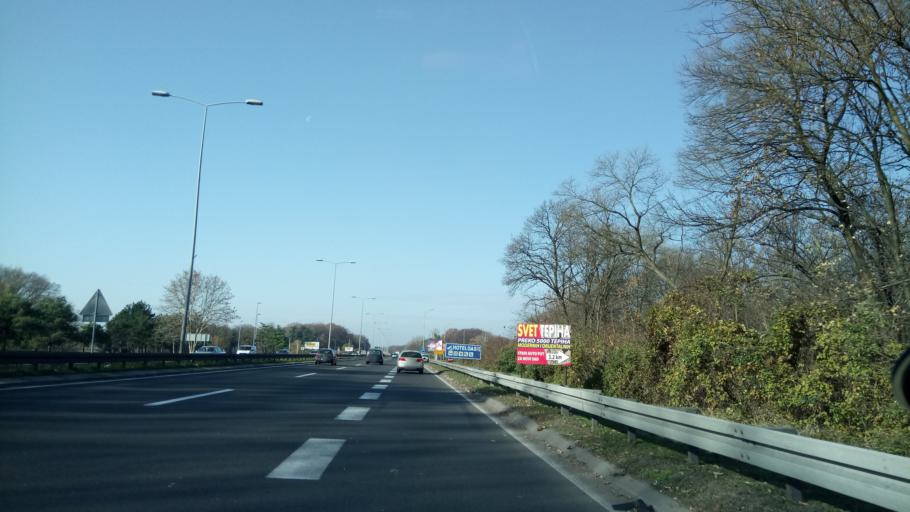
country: RS
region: Central Serbia
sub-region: Belgrade
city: Zemun
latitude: 44.8318
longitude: 20.3674
